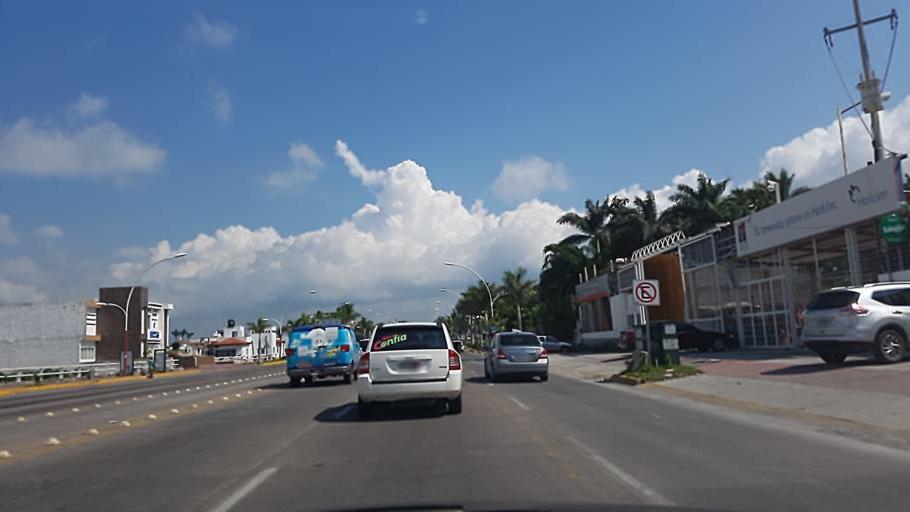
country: MX
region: Nayarit
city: Xalisco
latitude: 21.4788
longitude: -104.8916
